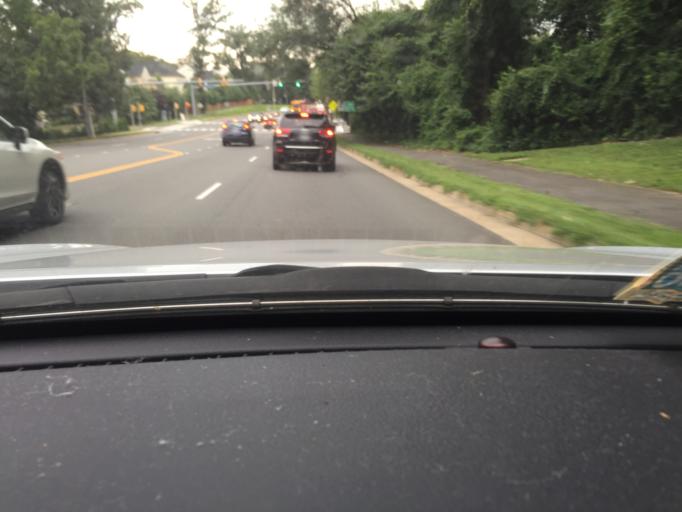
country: US
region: Virginia
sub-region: Fairfax County
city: Dunn Loring
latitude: 38.8875
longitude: -77.2270
